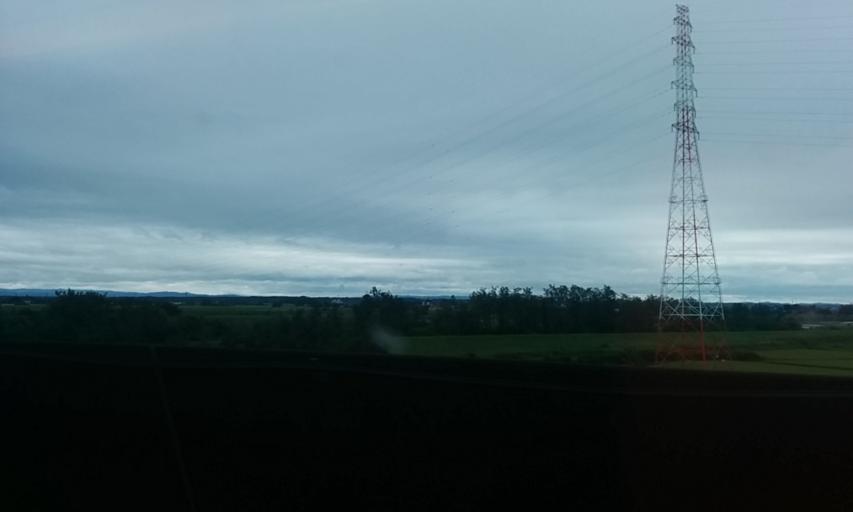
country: JP
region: Tochigi
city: Ujiie
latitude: 36.7026
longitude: 139.9199
